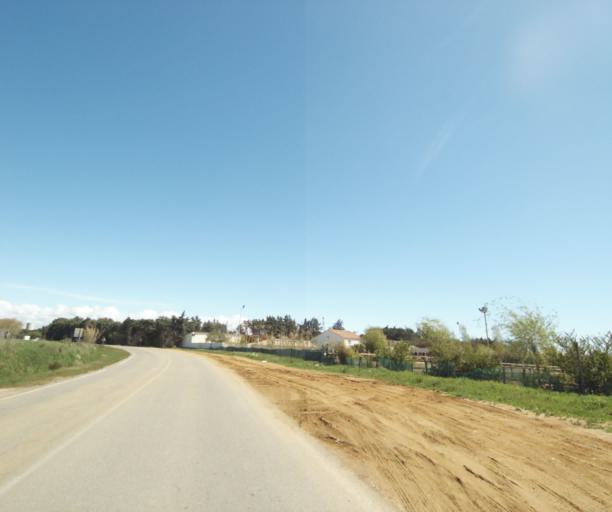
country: FR
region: Languedoc-Roussillon
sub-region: Departement de l'Herault
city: Villeneuve-les-Maguelone
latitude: 43.5564
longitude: 3.8614
